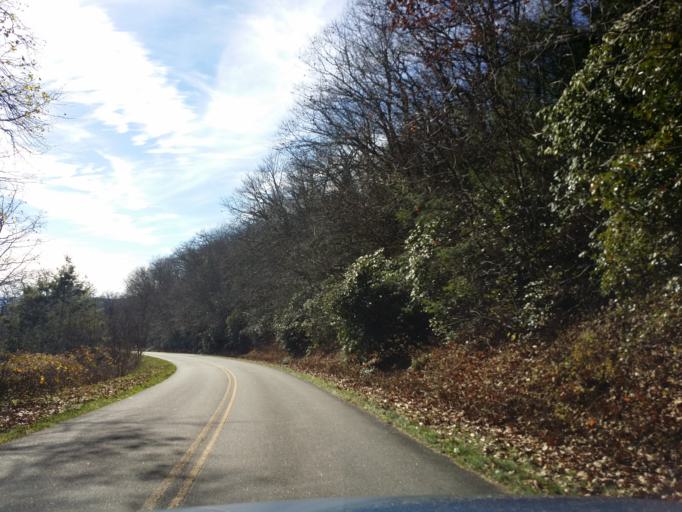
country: US
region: North Carolina
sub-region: Buncombe County
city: Black Mountain
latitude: 35.7181
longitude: -82.2283
